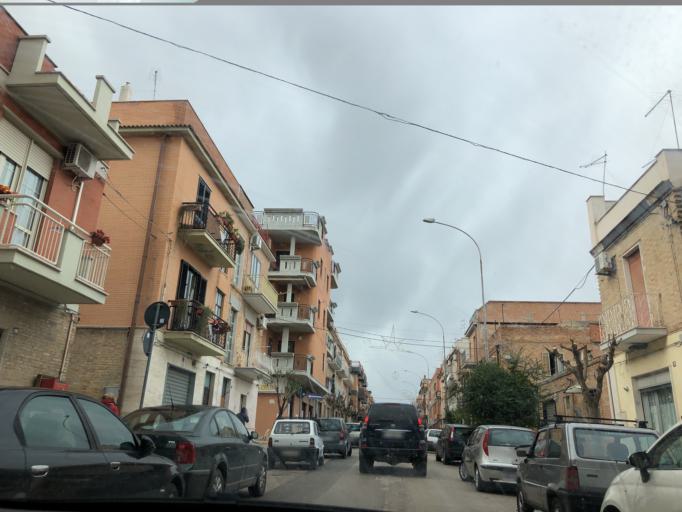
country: IT
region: Apulia
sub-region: Provincia di Foggia
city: Lucera
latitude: 41.5076
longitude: 15.3276
